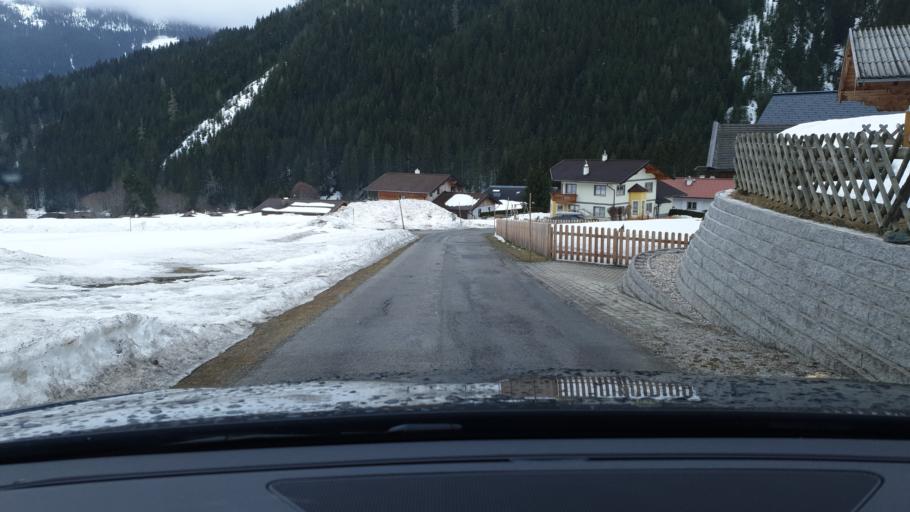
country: AT
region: Salzburg
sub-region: Politischer Bezirk Sankt Johann im Pongau
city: Filzmoos
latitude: 47.4464
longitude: 13.5216
